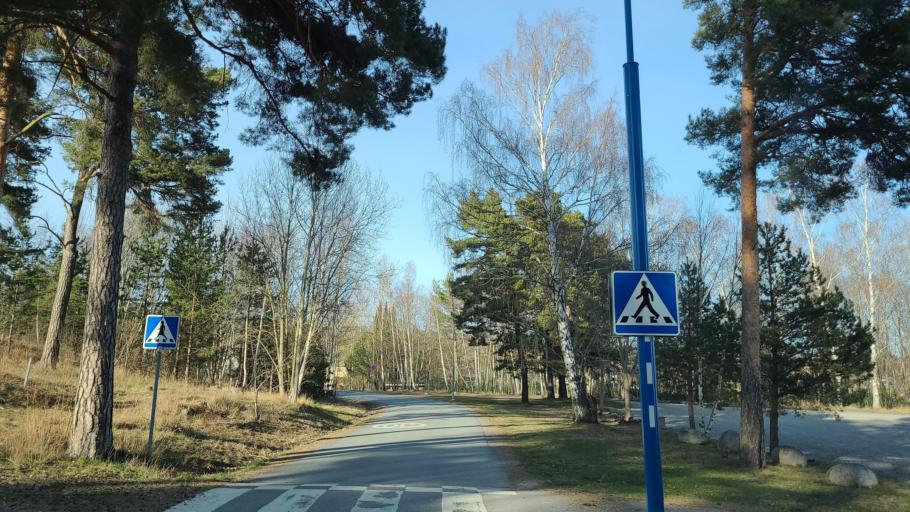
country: SE
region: Stockholm
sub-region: Ekero Kommun
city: Ekeroe
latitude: 59.2685
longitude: 17.7809
